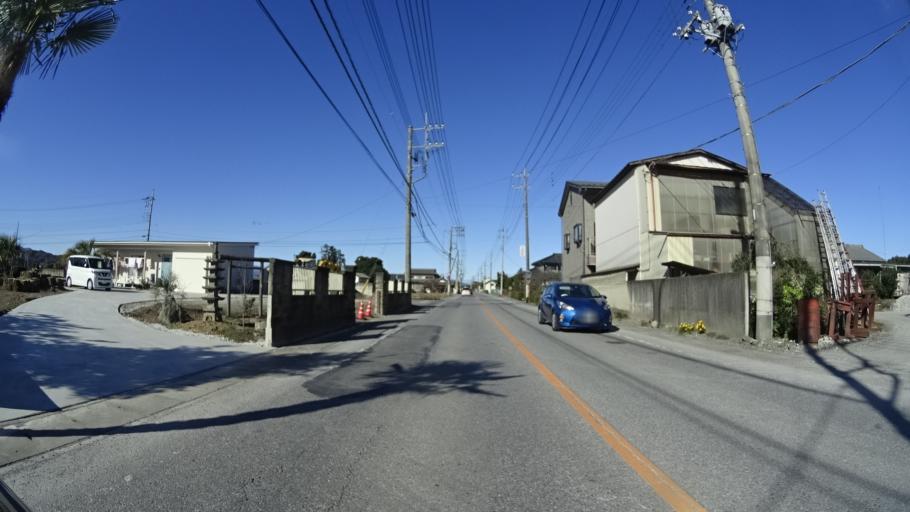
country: JP
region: Tochigi
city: Mibu
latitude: 36.4569
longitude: 139.7539
